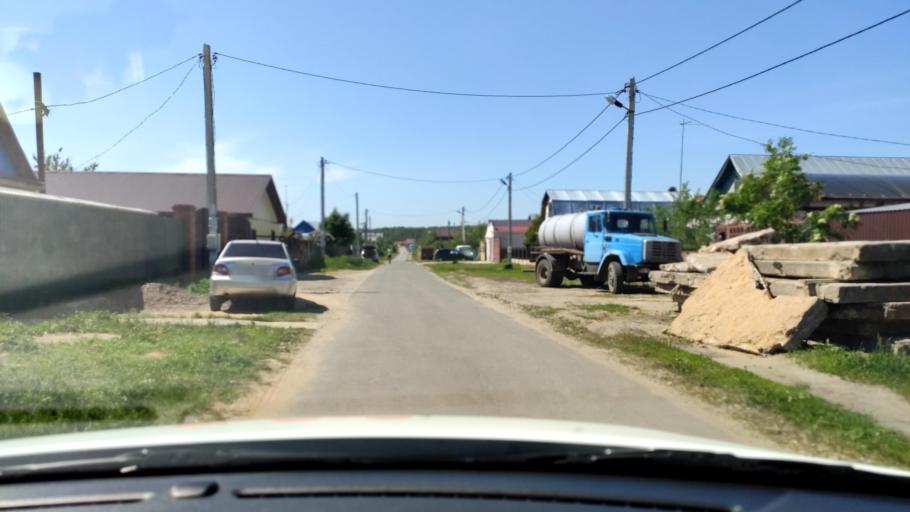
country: RU
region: Tatarstan
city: Osinovo
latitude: 55.8287
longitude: 48.8707
